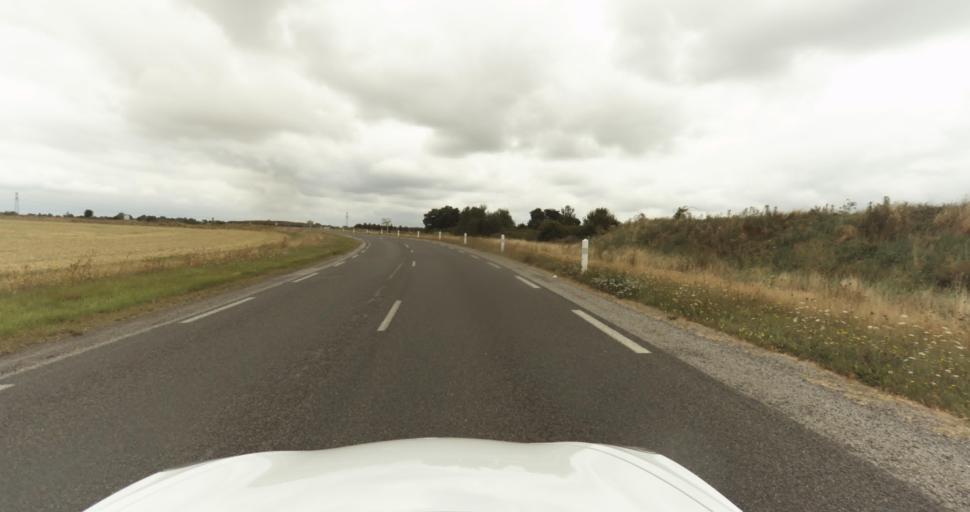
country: FR
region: Haute-Normandie
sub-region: Departement de l'Eure
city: Saint-Sebastien-de-Morsent
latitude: 49.0344
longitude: 1.0884
